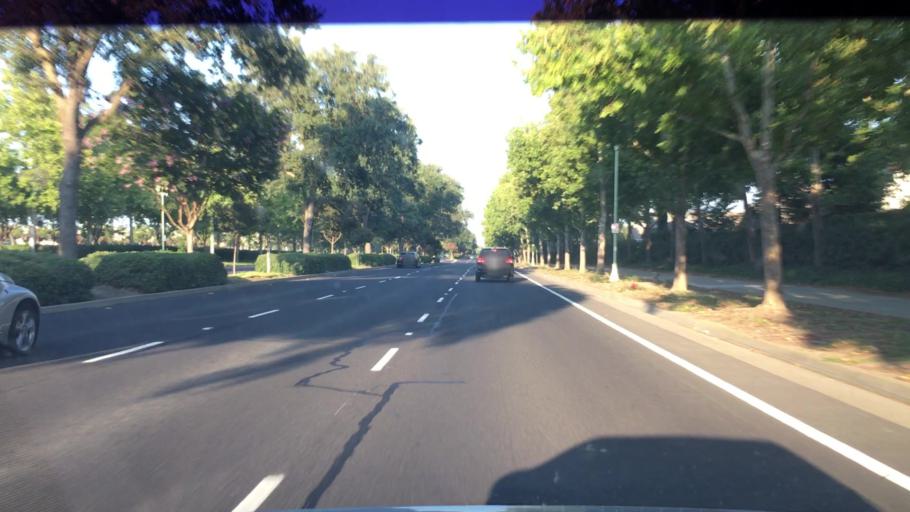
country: US
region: California
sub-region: Sacramento County
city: Laguna
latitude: 38.4279
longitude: -121.4786
